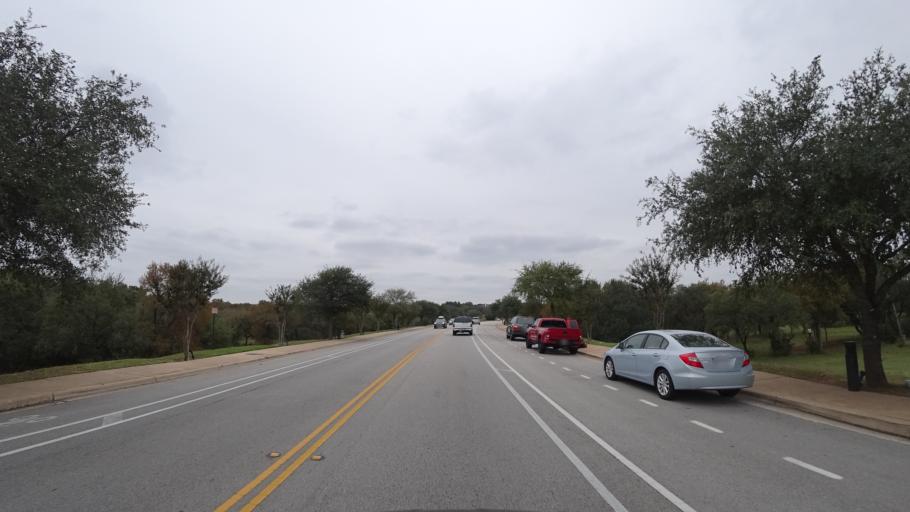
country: US
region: Texas
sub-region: Travis County
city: Shady Hollow
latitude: 30.1978
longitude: -97.8792
